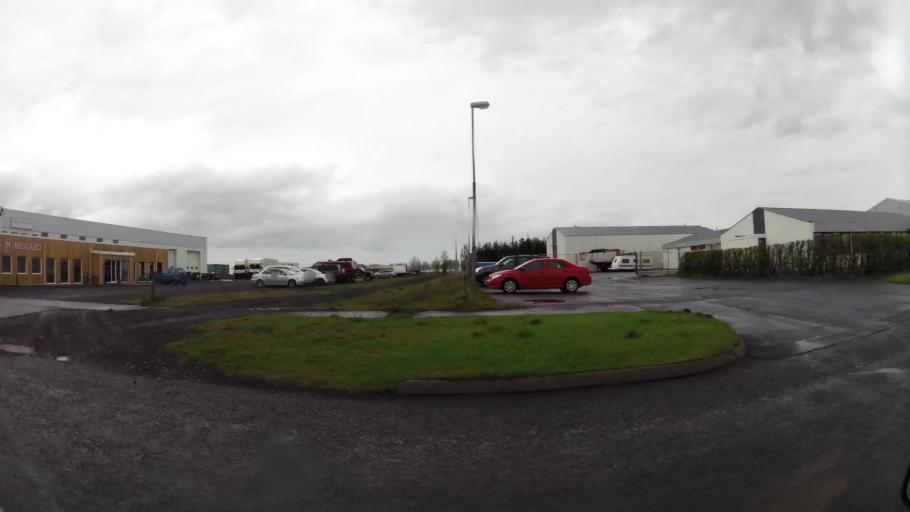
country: IS
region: South
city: Vestmannaeyjar
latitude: 63.7463
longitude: -20.2277
